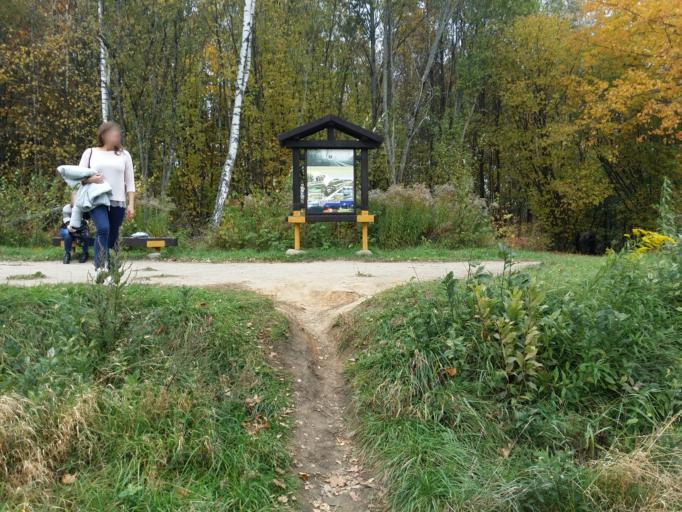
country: LT
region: Vilnius County
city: Rasos
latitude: 54.6837
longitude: 25.3690
